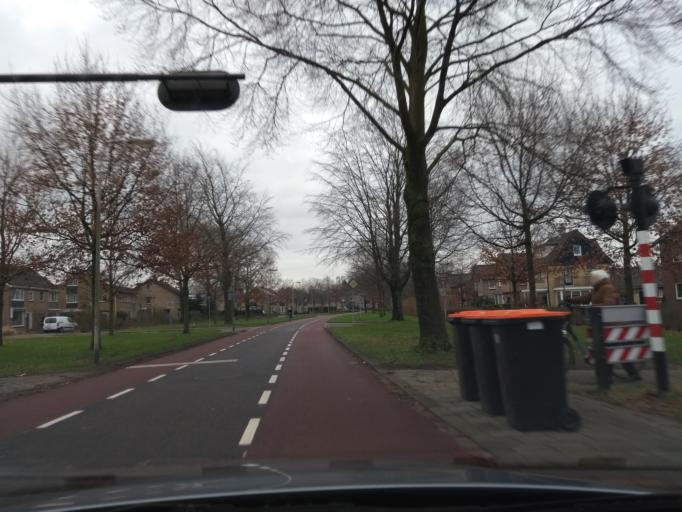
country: NL
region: Overijssel
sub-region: Gemeente Haaksbergen
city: Haaksbergen
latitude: 52.1627
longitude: 6.7478
